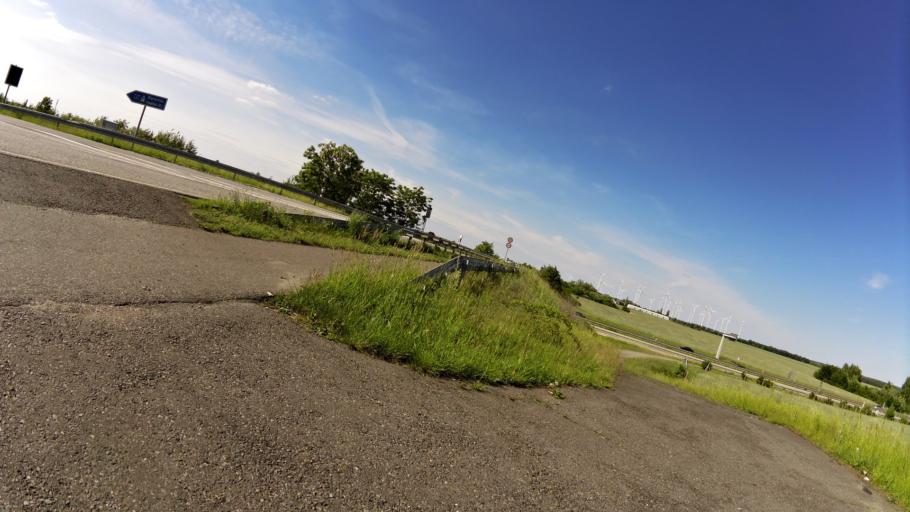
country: DE
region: Brandenburg
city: Jacobsdorf
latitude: 52.3211
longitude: 14.3518
